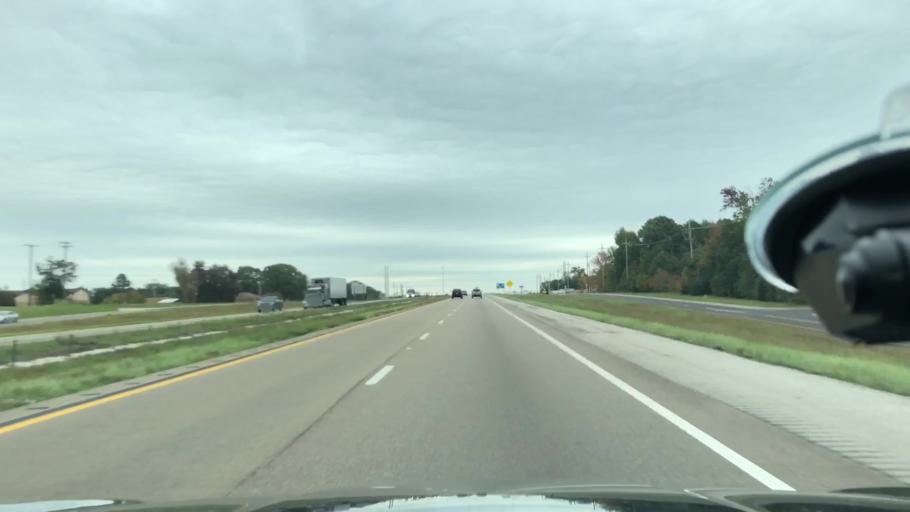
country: US
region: Texas
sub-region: Titus County
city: Mount Pleasant
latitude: 33.1727
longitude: -94.9899
